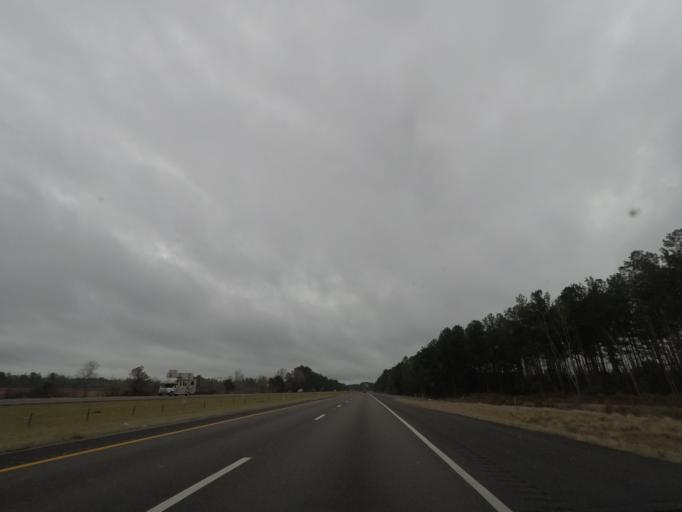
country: US
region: South Carolina
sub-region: Orangeburg County
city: Holly Hill
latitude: 33.4575
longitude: -80.4793
